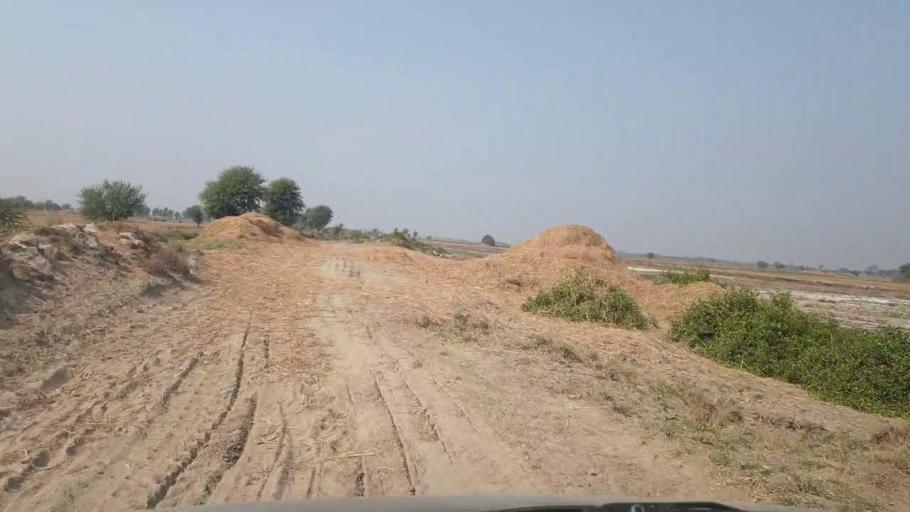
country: PK
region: Sindh
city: Tando Muhammad Khan
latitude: 25.0688
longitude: 68.3578
